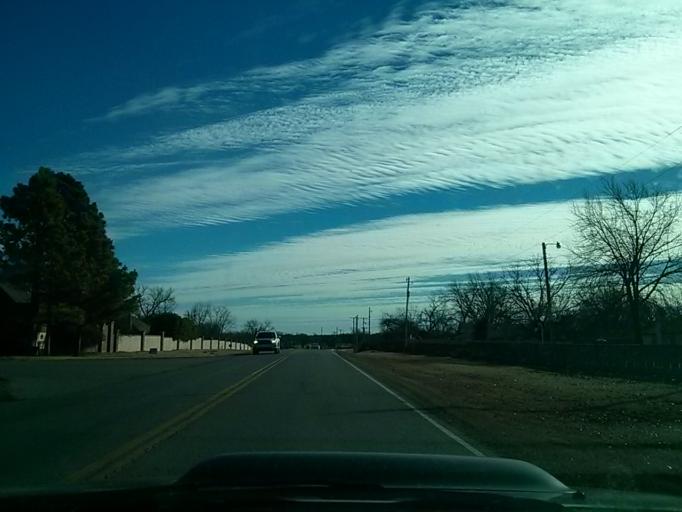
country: US
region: Oklahoma
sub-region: Tulsa County
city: Jenks
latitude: 36.0245
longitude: -96.0009
